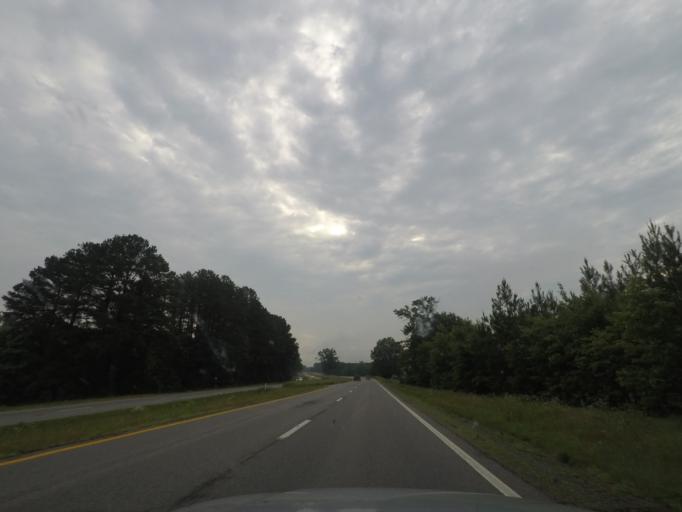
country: US
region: Virginia
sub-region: Mecklenburg County
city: Chase City
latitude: 36.8692
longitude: -78.5748
